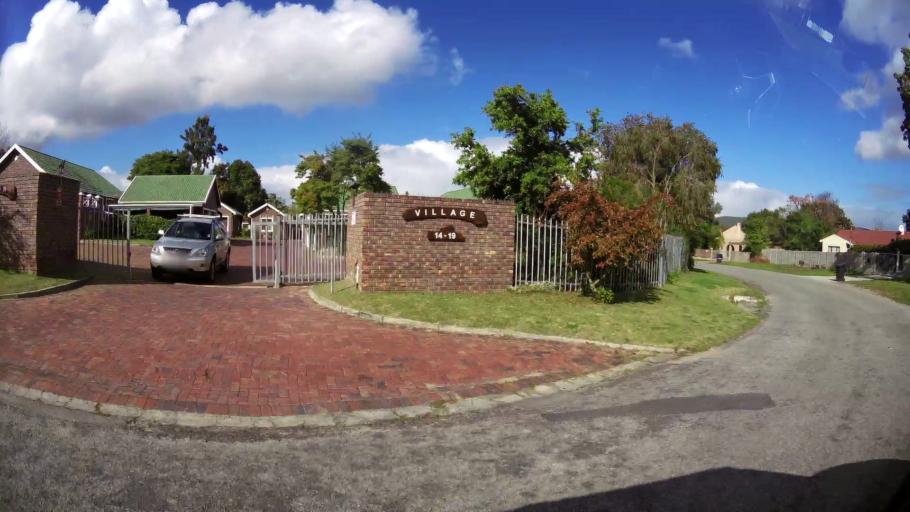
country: ZA
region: Western Cape
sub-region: Eden District Municipality
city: Knysna
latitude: -34.0413
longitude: 23.0689
